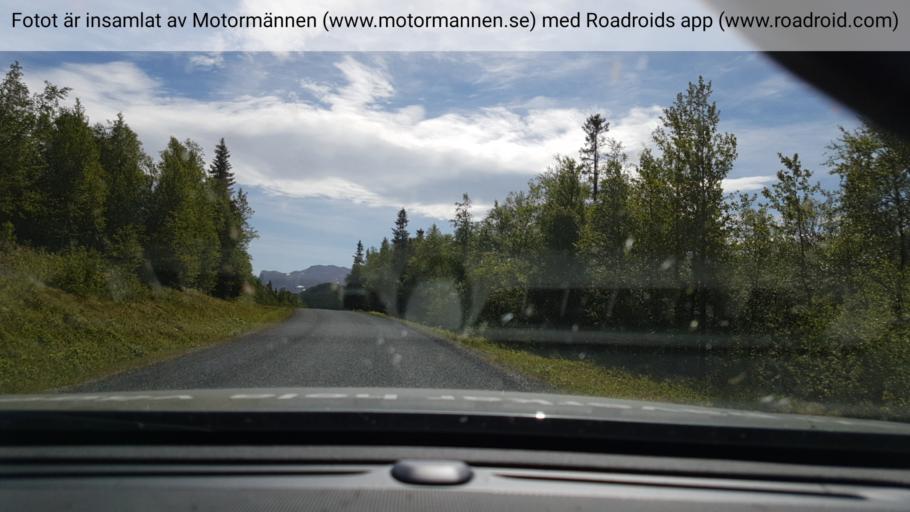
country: SE
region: Vaesterbotten
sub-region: Vilhelmina Kommun
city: Sjoberg
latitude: 65.2833
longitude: 15.2978
